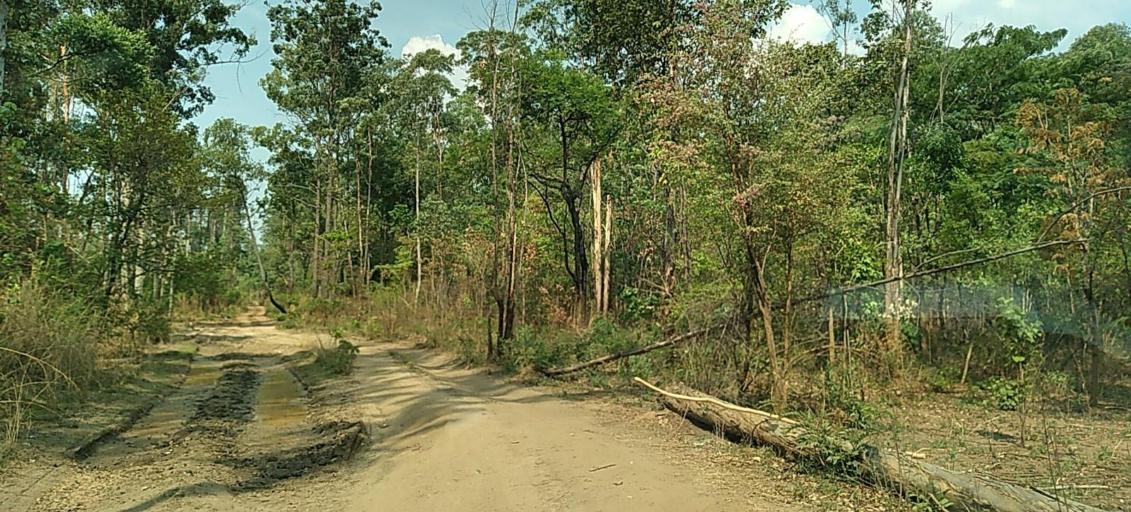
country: ZM
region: Copperbelt
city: Chingola
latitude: -12.7396
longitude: 27.7530
